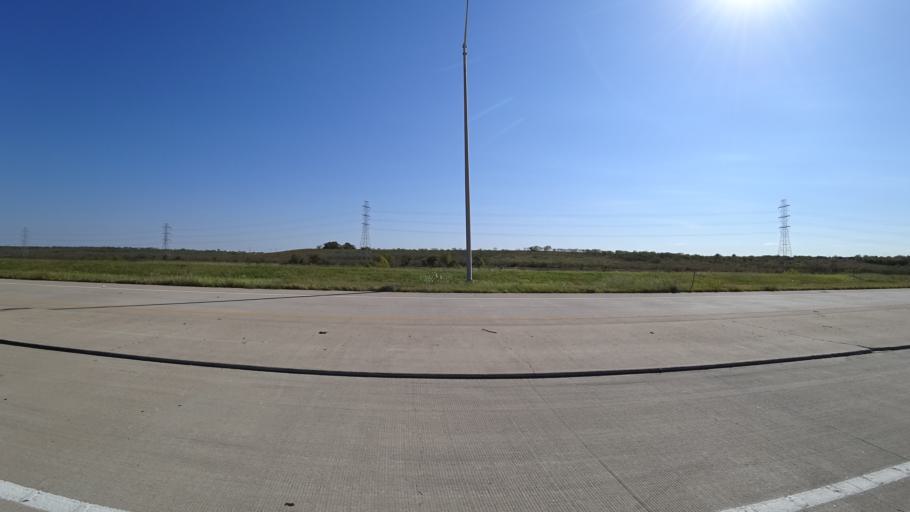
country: US
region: Texas
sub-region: Travis County
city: Garfield
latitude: 30.1809
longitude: -97.6311
